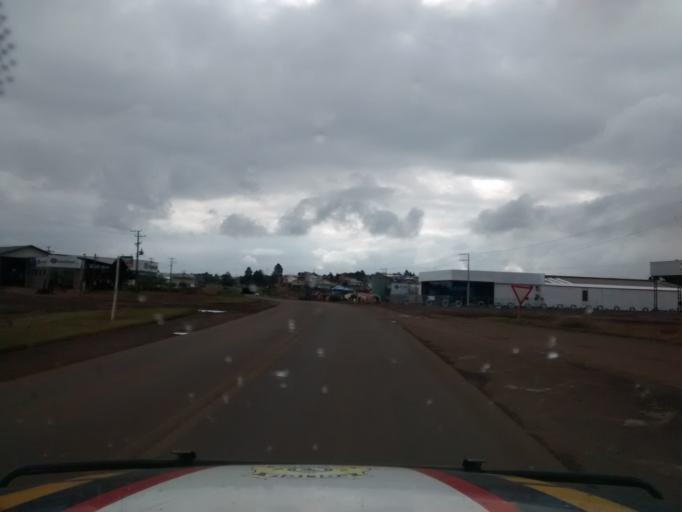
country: BR
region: Rio Grande do Sul
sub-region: Lagoa Vermelha
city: Lagoa Vermelha
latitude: -28.2104
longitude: -51.5115
